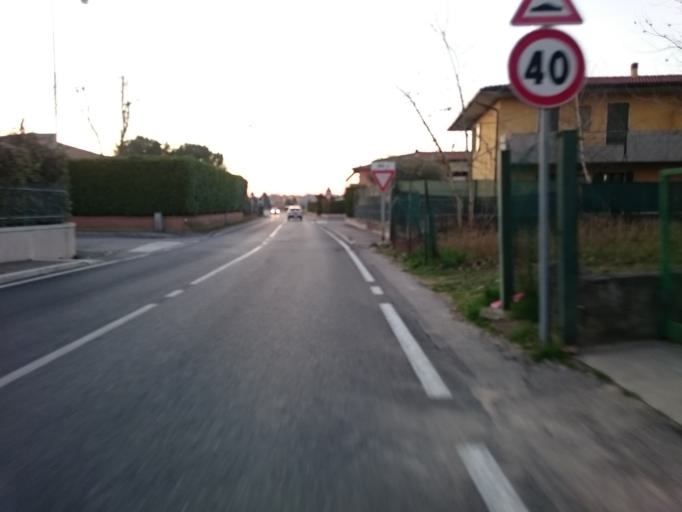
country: IT
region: Veneto
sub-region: Provincia di Verona
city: Salionze
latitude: 45.4073
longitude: 10.7502
